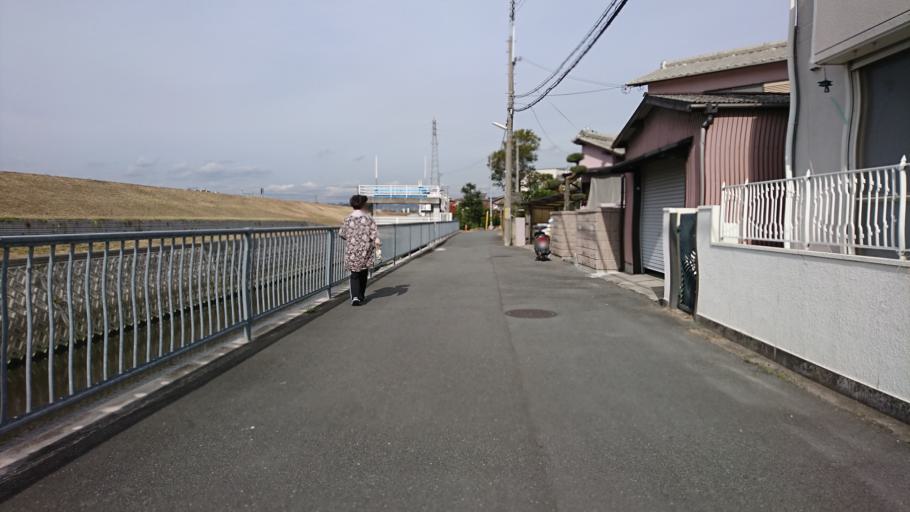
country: JP
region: Hyogo
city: Kakogawacho-honmachi
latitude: 34.7512
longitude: 134.8126
